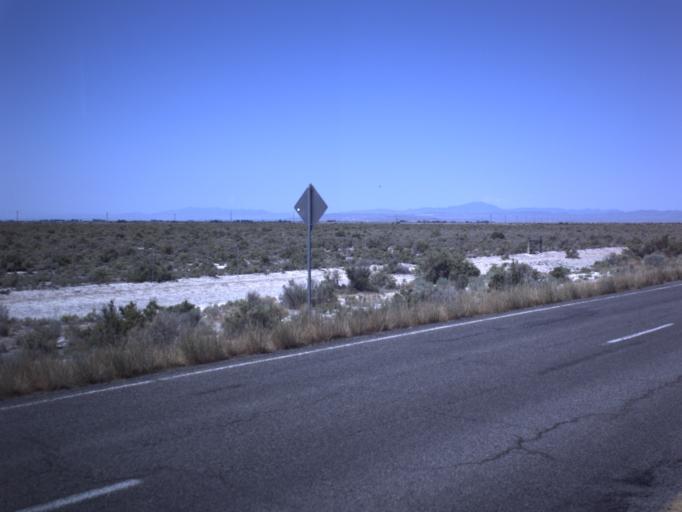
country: US
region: Utah
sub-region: Millard County
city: Delta
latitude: 39.4939
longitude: -112.5731
